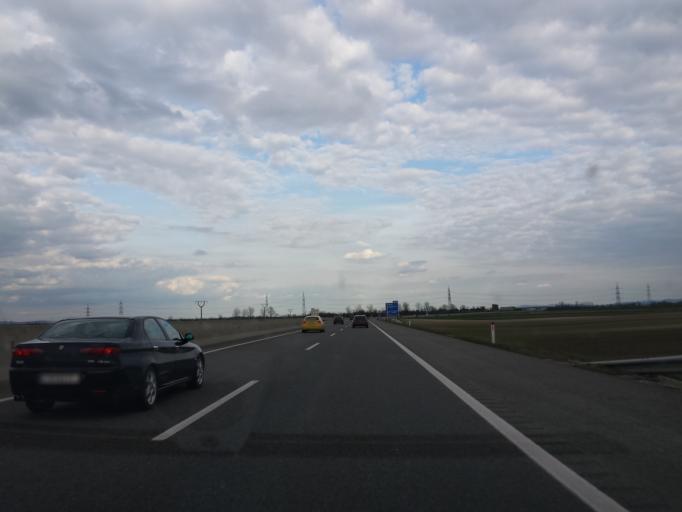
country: AT
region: Lower Austria
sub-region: Politischer Bezirk Tulln
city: Kirchberg am Wagram
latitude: 48.4100
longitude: 15.8629
